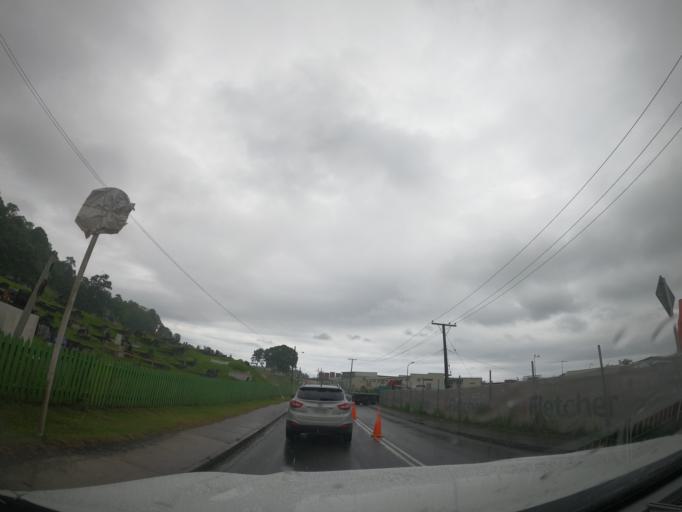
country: FJ
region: Central
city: Suva
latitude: -18.1160
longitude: 178.4312
